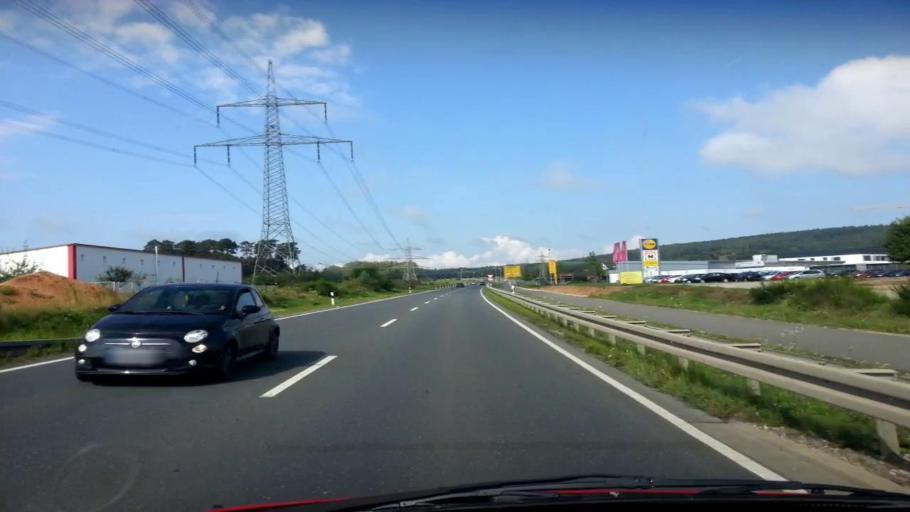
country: DE
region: Bavaria
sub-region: Upper Franconia
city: Hausen
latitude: 49.6960
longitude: 11.0401
